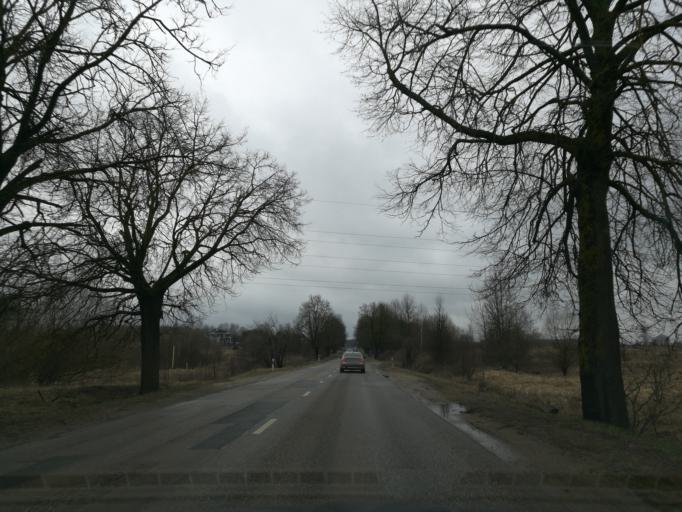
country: LT
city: Grigiskes
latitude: 54.6466
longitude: 25.1337
